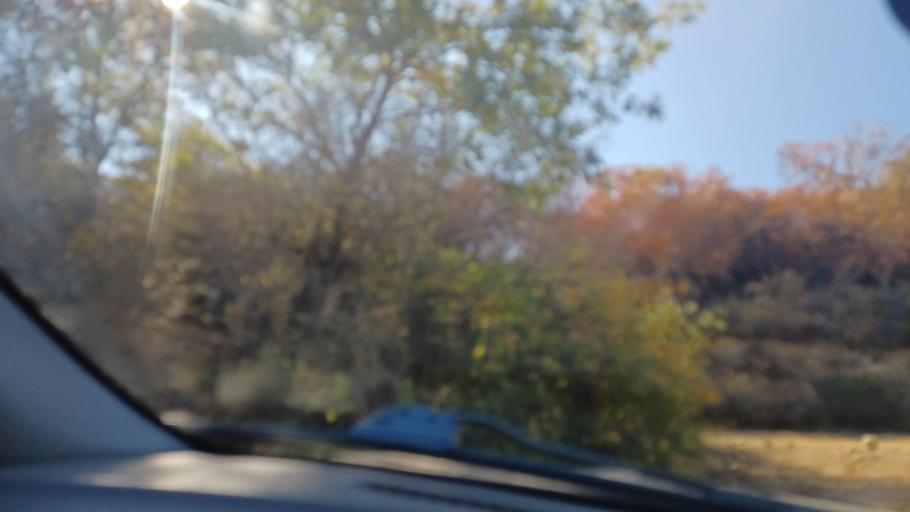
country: CY
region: Pafos
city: Polis
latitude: 34.9442
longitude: 32.4851
